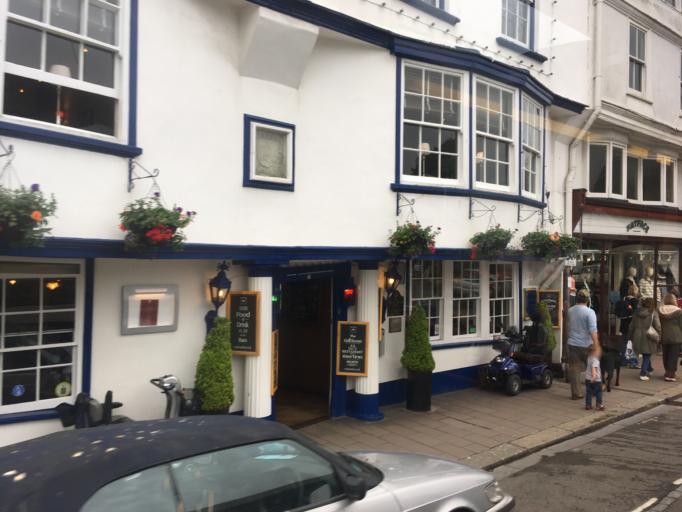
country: GB
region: England
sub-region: Devon
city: Dartmouth
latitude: 50.3515
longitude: -3.5784
